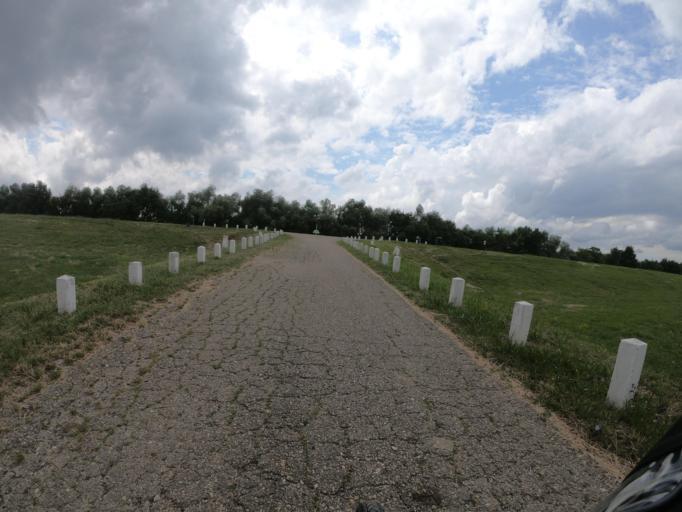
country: HU
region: Jasz-Nagykun-Szolnok
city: Tiszafured
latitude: 47.6819
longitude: 20.7440
